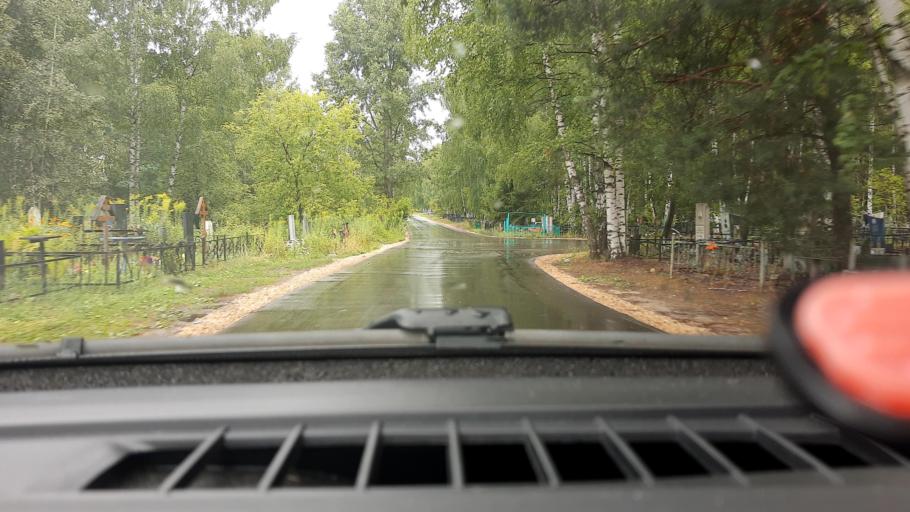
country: RU
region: Nizjnij Novgorod
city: Gorbatovka
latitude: 56.3563
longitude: 43.7776
